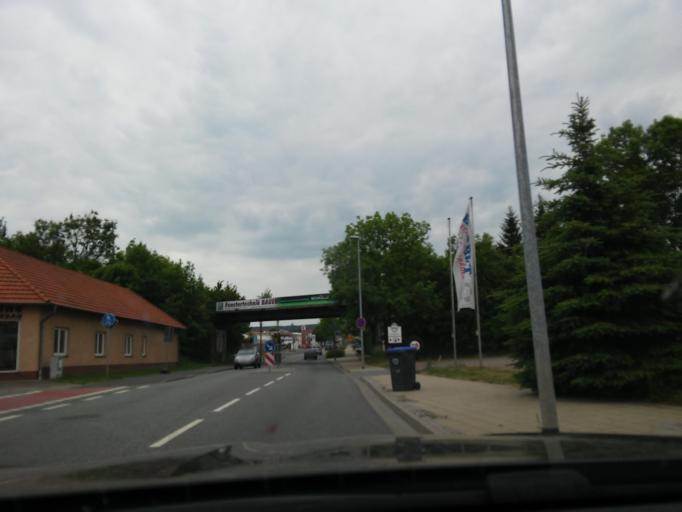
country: DE
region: Thuringia
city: Sondershausen
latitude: 51.3660
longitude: 10.8472
